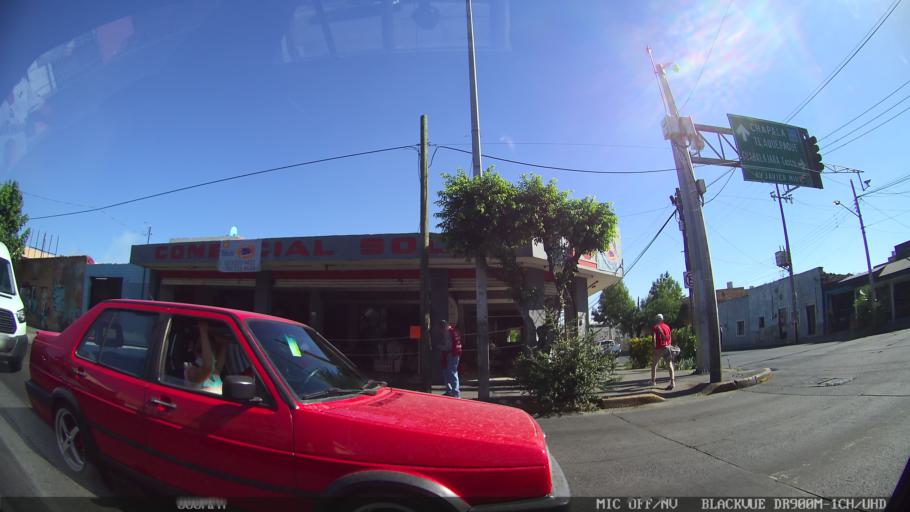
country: MX
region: Jalisco
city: Tlaquepaque
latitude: 20.6679
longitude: -103.3148
